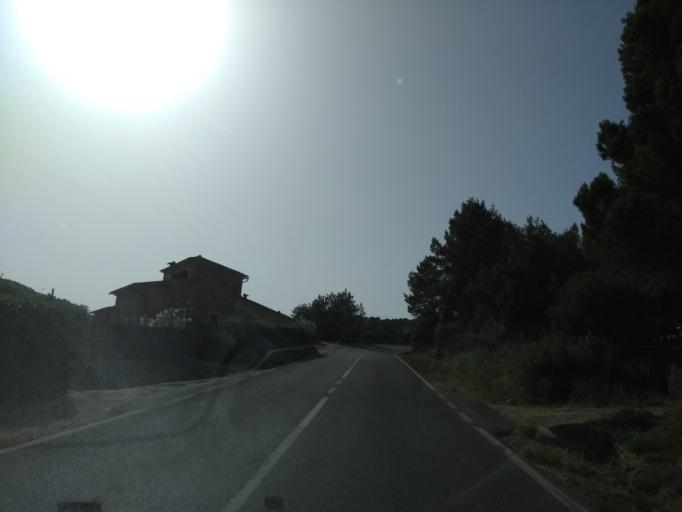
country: ES
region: Balearic Islands
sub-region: Illes Balears
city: Soller
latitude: 39.7819
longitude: 2.7117
